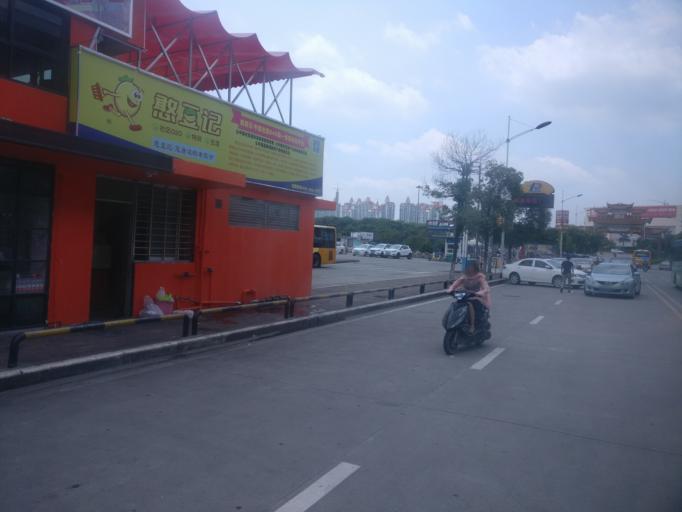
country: CN
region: Guangdong
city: Dashi
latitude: 23.0406
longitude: 113.3148
